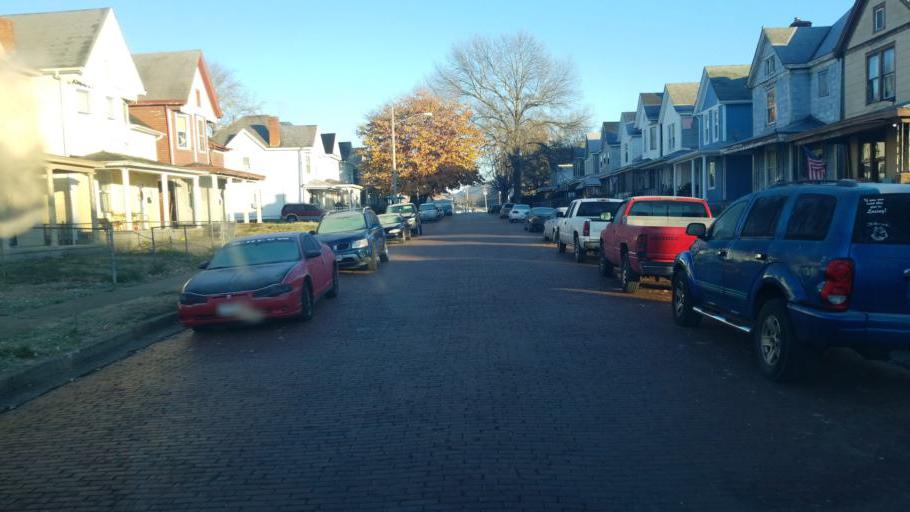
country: US
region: Kentucky
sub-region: Greenup County
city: South Shore
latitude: 38.7412
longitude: -82.9708
